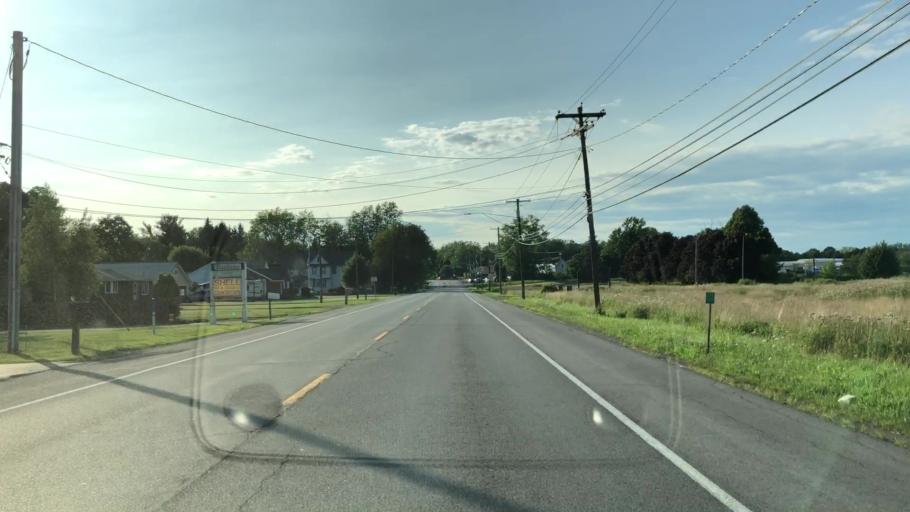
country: US
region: New York
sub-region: Erie County
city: West Seneca
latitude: 42.8657
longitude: -78.7725
